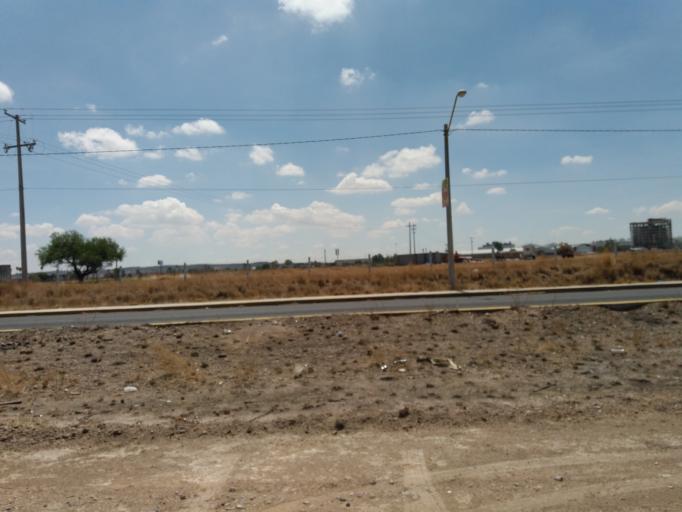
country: MX
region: Aguascalientes
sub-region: Aguascalientes
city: San Sebastian [Fraccionamiento]
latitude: 21.8124
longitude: -102.2926
